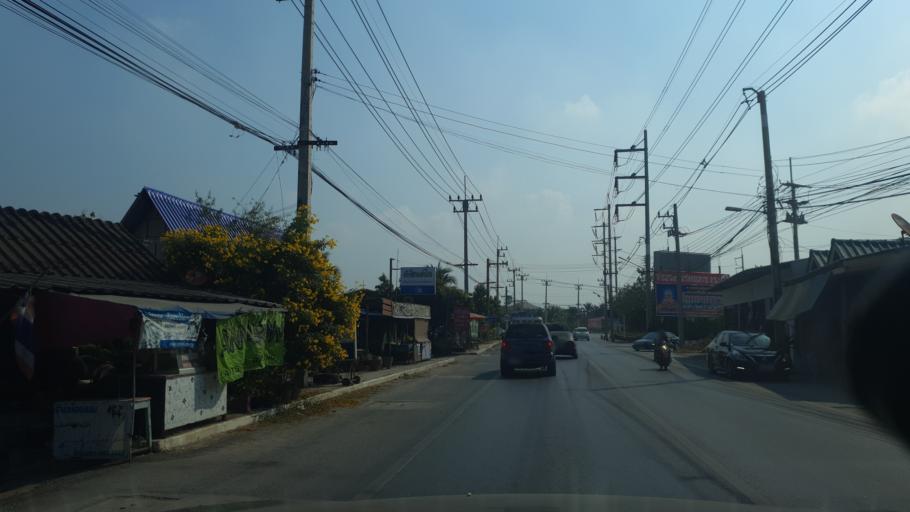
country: TH
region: Nakhon Pathom
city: Salaya
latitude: 13.7736
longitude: 100.2834
